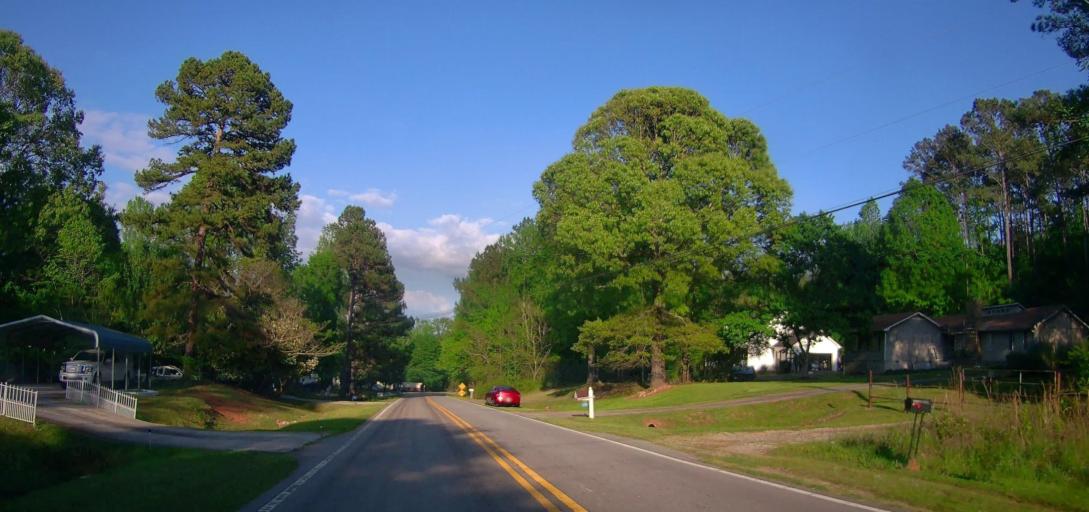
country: US
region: Georgia
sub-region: Putnam County
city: Eatonton
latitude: 33.3160
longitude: -83.3692
